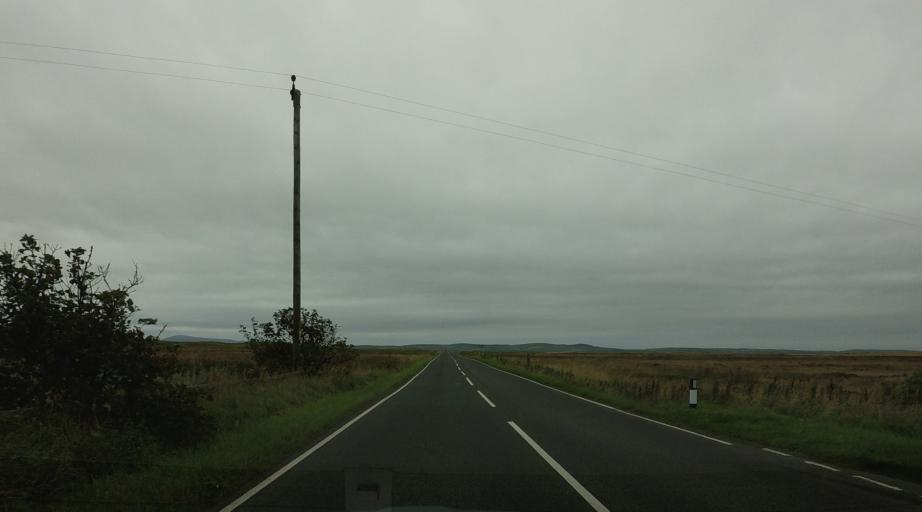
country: GB
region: Scotland
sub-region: Orkney Islands
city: Stromness
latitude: 59.0049
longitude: -3.1544
